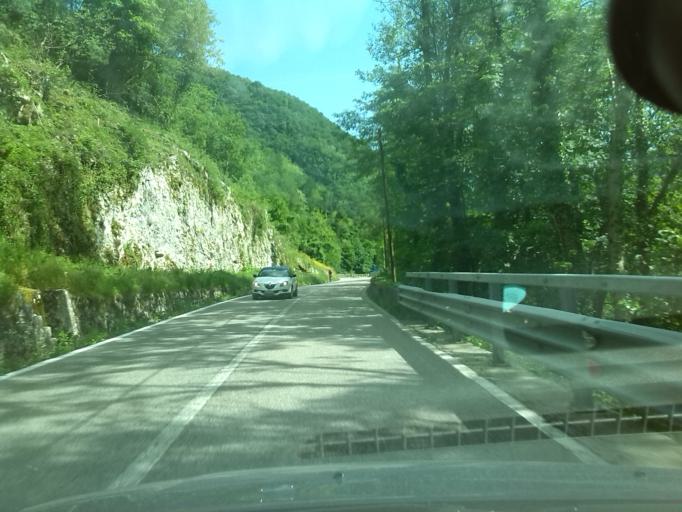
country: IT
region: Friuli Venezia Giulia
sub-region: Provincia di Udine
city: Pulfero
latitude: 46.1849
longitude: 13.4762
